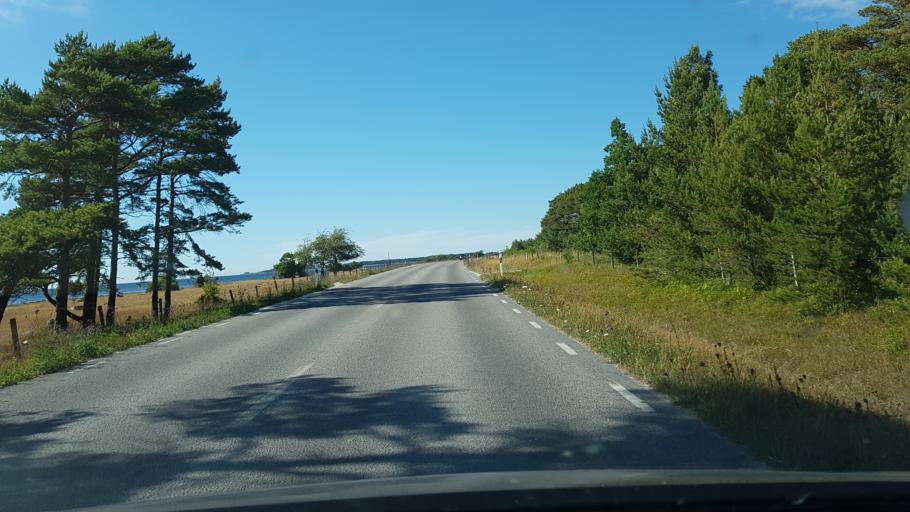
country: SE
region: Gotland
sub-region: Gotland
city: Klintehamn
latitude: 57.4179
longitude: 18.1517
